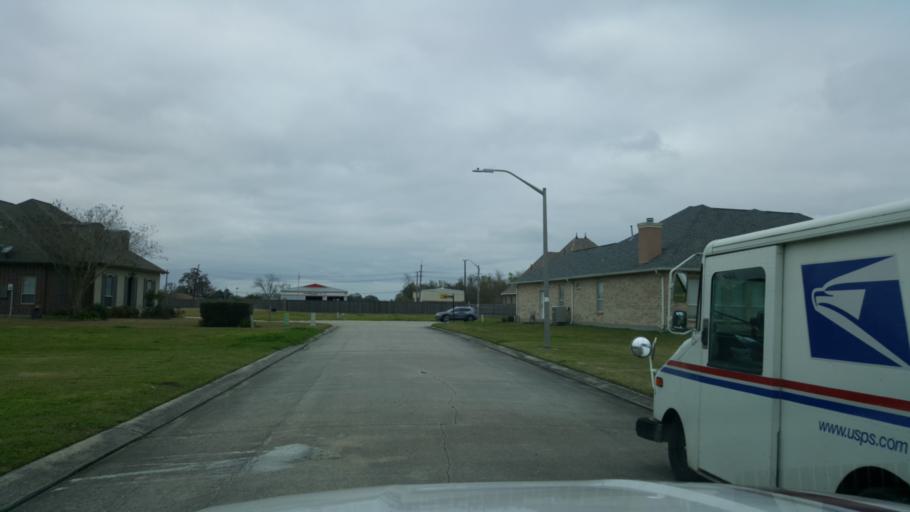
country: US
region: Louisiana
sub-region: Jefferson Parish
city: Woodmere
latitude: 29.8803
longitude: -90.0823
